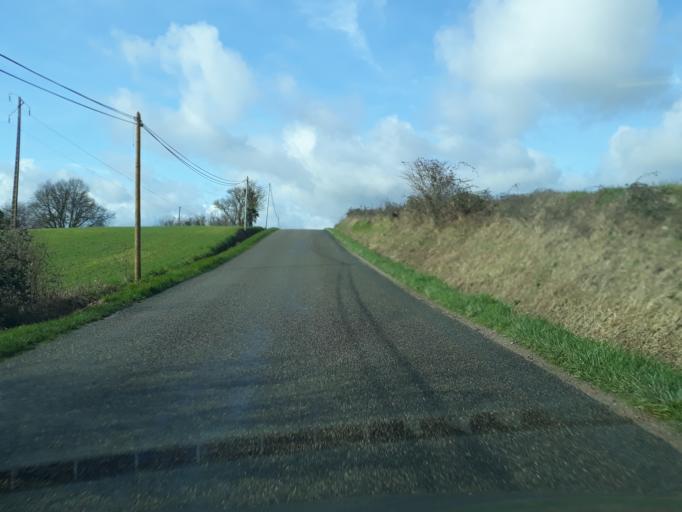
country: FR
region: Midi-Pyrenees
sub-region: Departement du Gers
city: Pujaudran
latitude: 43.6189
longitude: 1.0425
